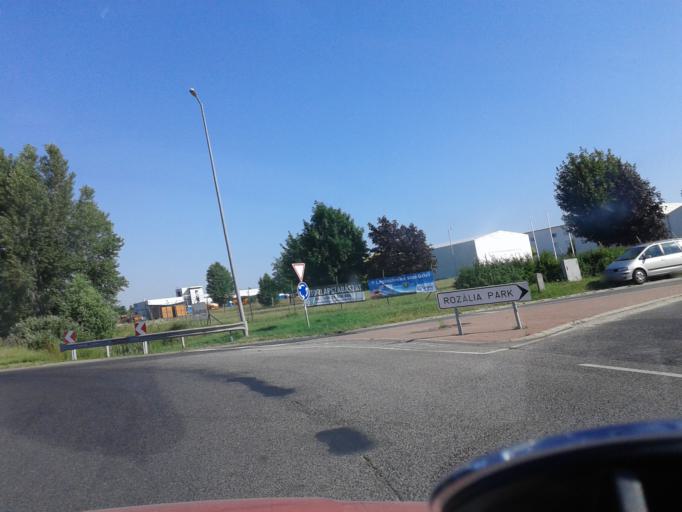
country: HU
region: Pest
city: Biatorbagy
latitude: 47.4752
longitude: 18.8437
